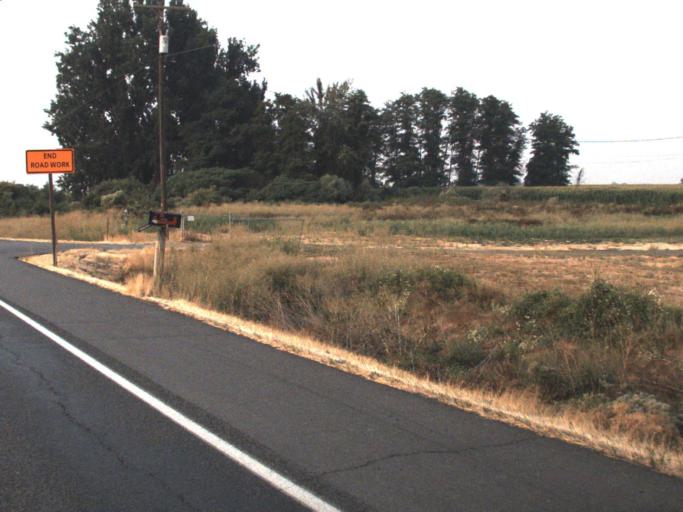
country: US
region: Washington
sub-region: Yakima County
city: Toppenish
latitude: 46.3547
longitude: -120.3204
